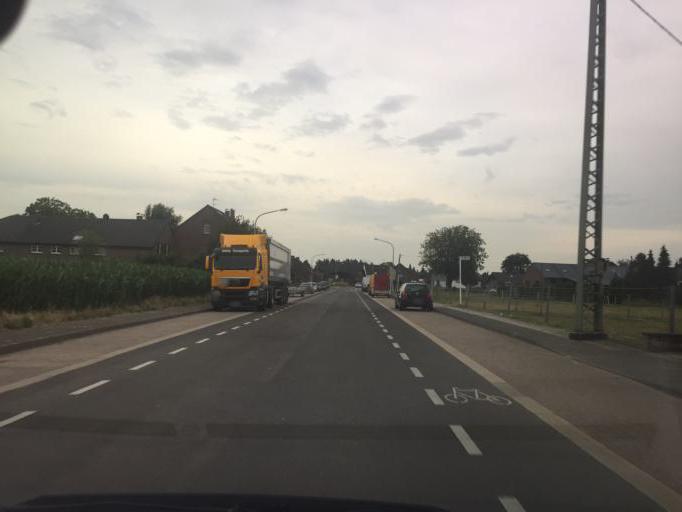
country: DE
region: North Rhine-Westphalia
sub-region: Regierungsbezirk Dusseldorf
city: Monchengladbach
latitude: 51.1753
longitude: 6.3721
